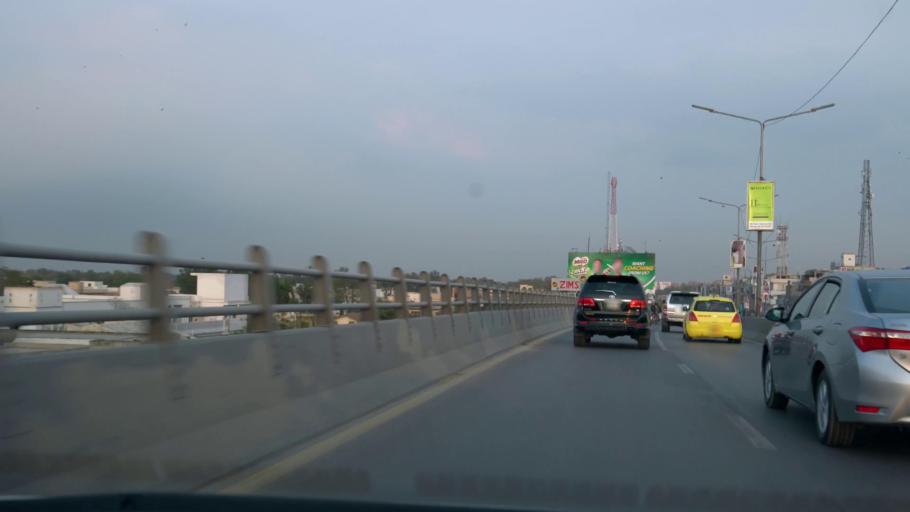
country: PK
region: Punjab
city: Lahore
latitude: 31.5022
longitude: 74.3566
